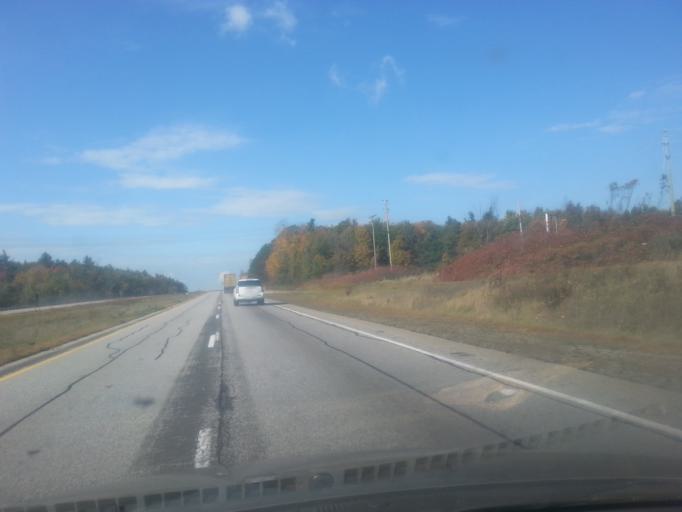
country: US
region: New York
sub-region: Jefferson County
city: Alexandria Bay
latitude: 44.3780
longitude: -76.0090
